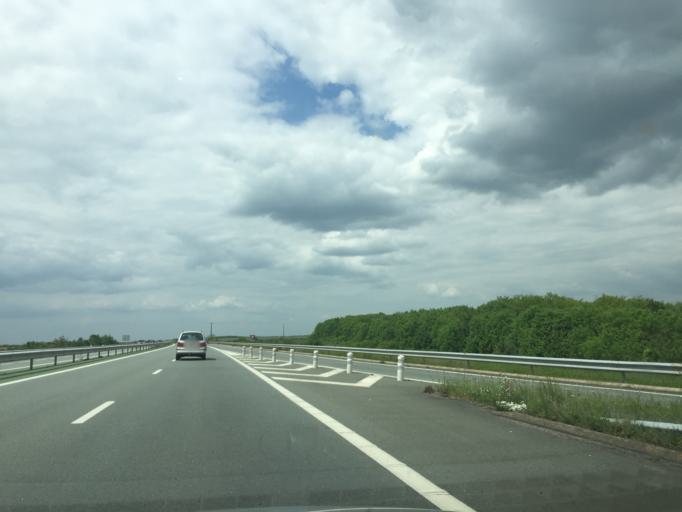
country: FR
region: Poitou-Charentes
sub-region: Departement des Deux-Sevres
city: Echire
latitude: 46.4156
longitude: -0.3996
